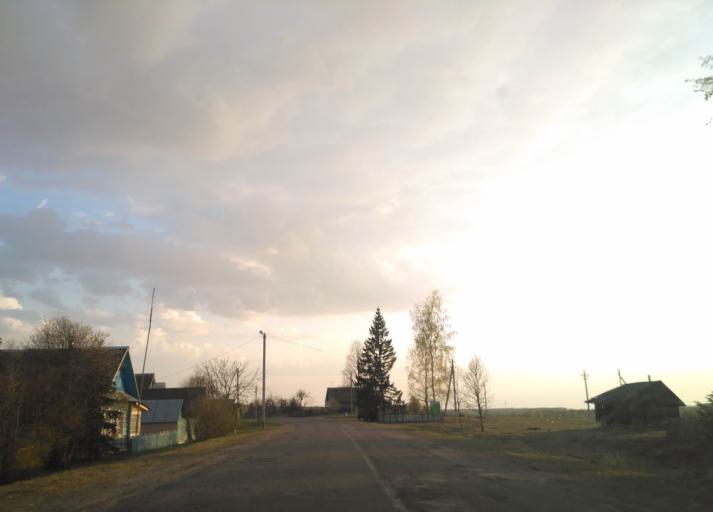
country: BY
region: Minsk
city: Loshnitsa
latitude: 54.4142
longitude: 28.6321
